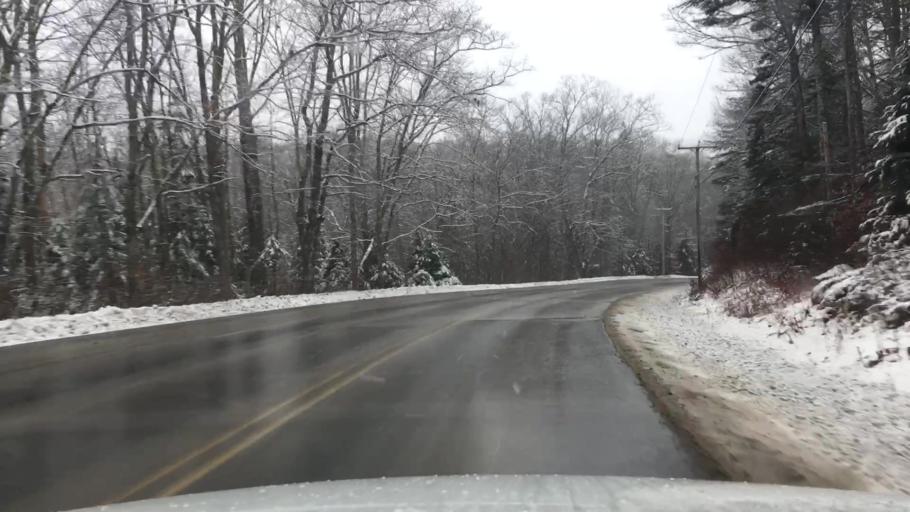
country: US
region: Maine
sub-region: Knox County
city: Warren
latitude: 44.1378
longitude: -69.2705
